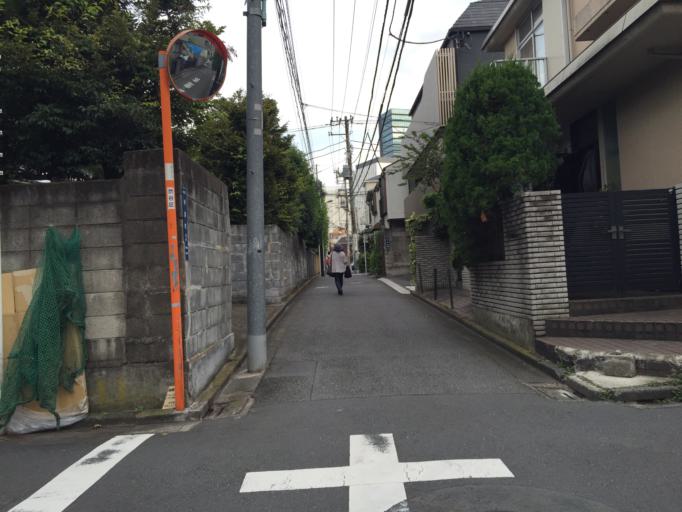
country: JP
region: Tokyo
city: Tokyo
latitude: 35.6579
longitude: 139.6924
